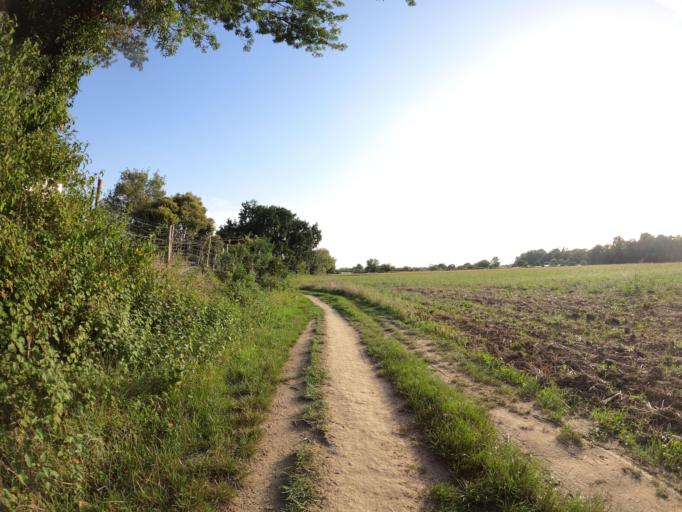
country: FR
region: Midi-Pyrenees
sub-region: Departement de la Haute-Garonne
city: Portet-sur-Garonne
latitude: 43.5417
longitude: 1.4240
